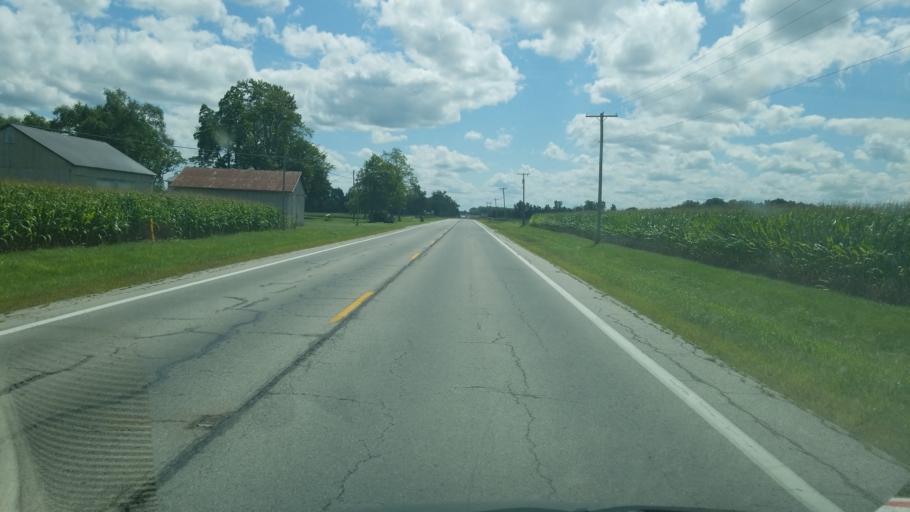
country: US
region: Ohio
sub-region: Henry County
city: Holgate
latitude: 41.3140
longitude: -84.1182
